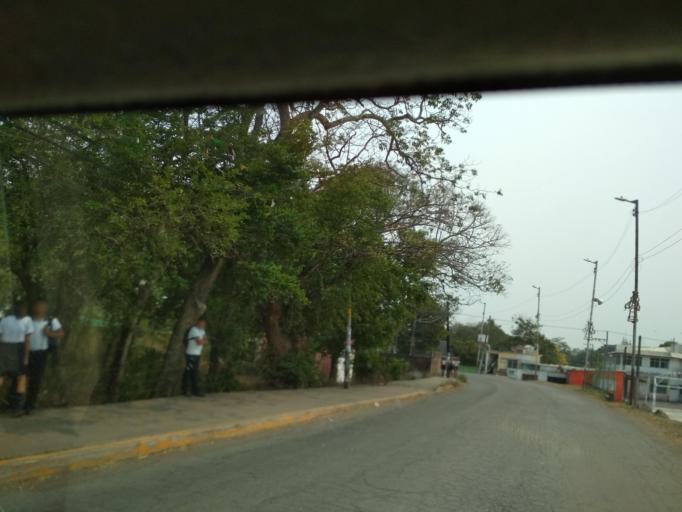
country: MX
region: Veracruz
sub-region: Veracruz
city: Delfino Victoria (Santa Fe)
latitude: 19.2069
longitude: -96.2736
